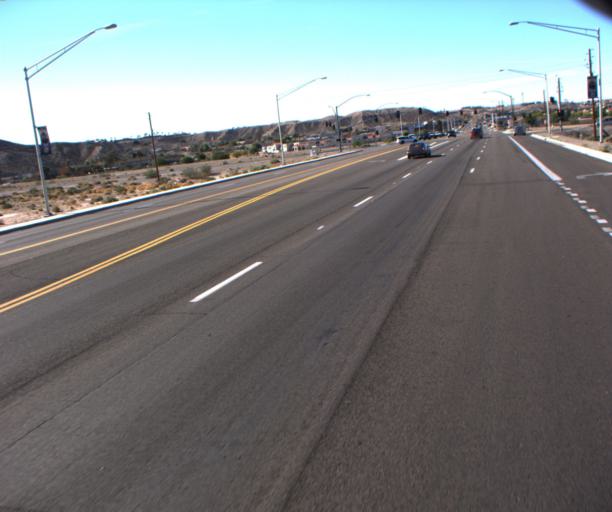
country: US
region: Arizona
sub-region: Mohave County
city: Bullhead City
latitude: 35.0576
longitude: -114.5893
